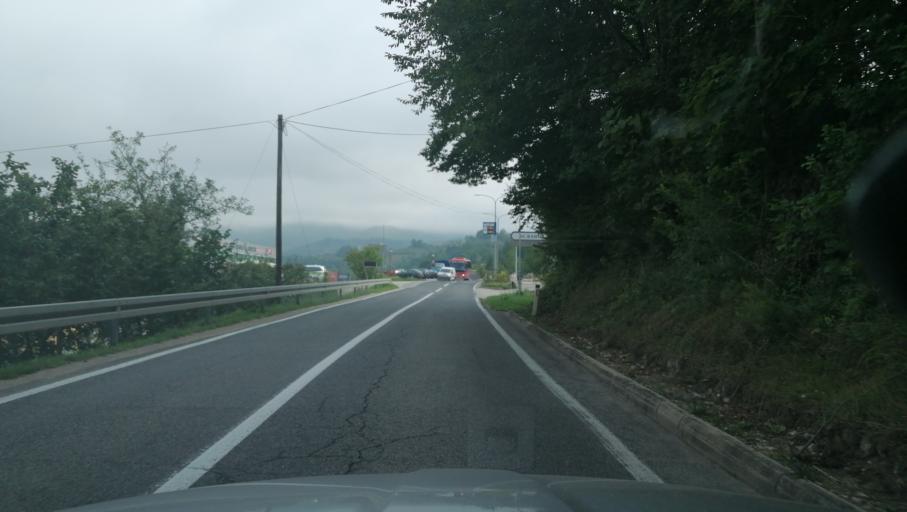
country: BA
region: Federation of Bosnia and Herzegovina
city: Jajce
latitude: 44.3515
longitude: 17.2985
